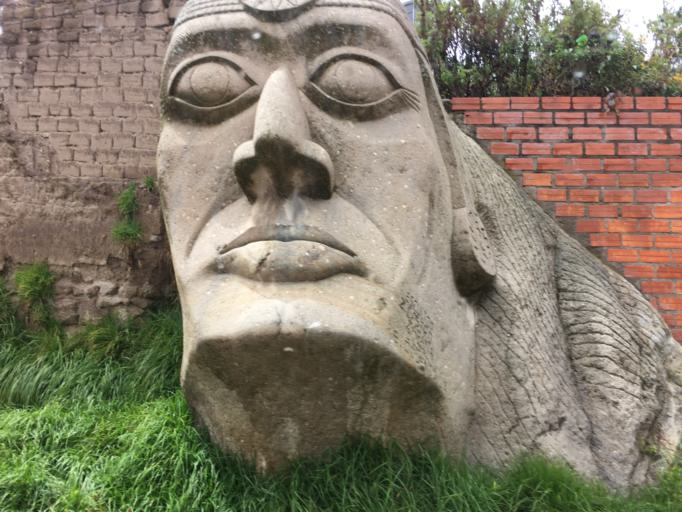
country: PE
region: Puno
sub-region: Yunguyo
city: Yunguyo
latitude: -16.1691
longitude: -69.0884
